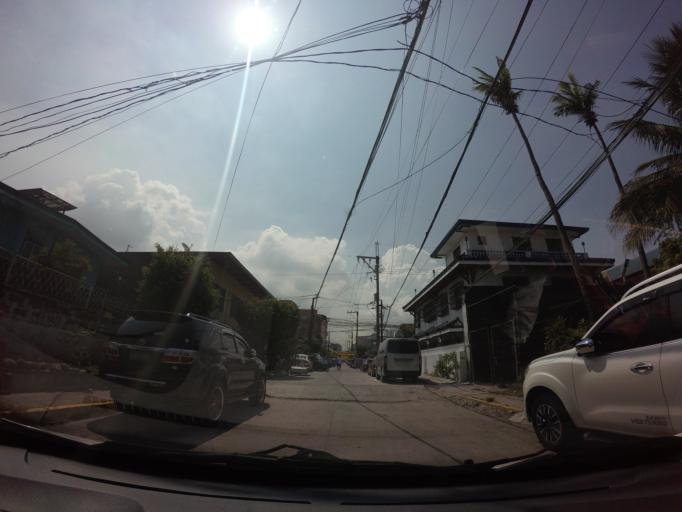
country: PH
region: Metro Manila
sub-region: Makati City
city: Makati City
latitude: 14.5718
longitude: 121.0113
